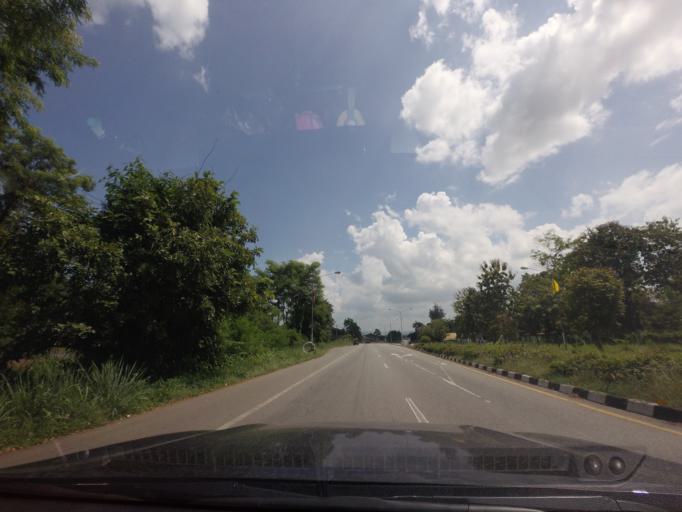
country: TH
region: Phetchabun
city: Phetchabun
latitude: 16.2511
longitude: 101.0670
